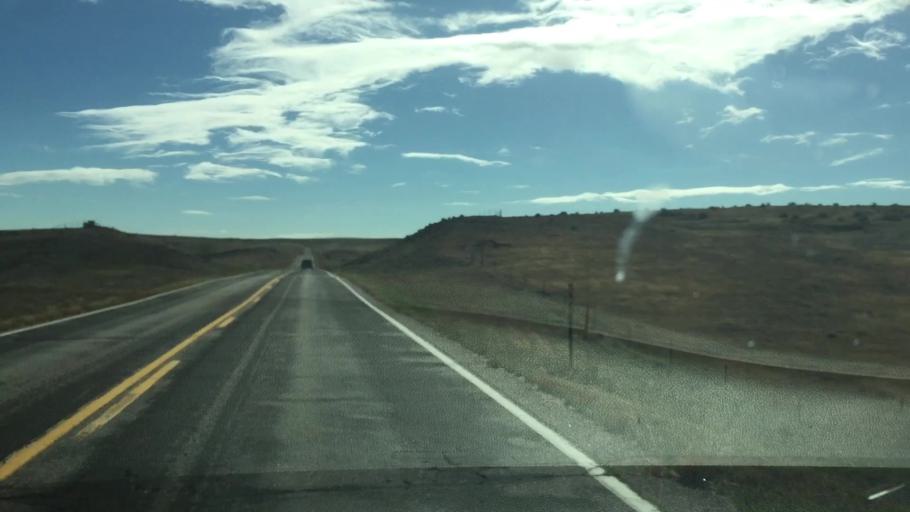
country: US
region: Colorado
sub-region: Elbert County
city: Kiowa
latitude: 39.2788
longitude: -104.2711
